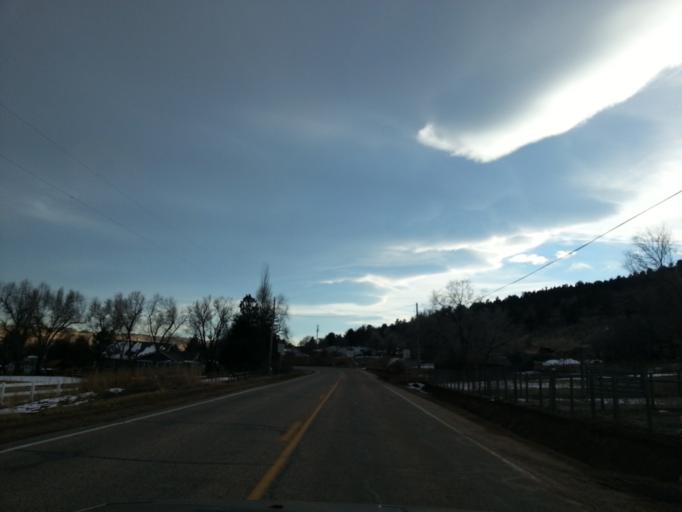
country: US
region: Colorado
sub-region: Larimer County
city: Loveland
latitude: 40.4268
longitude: -105.1930
